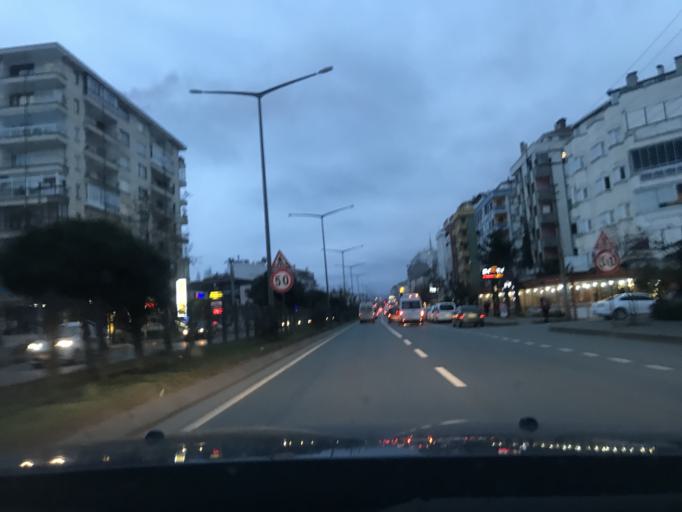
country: TR
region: Trabzon
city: Akcaabat
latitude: 41.0144
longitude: 39.6005
